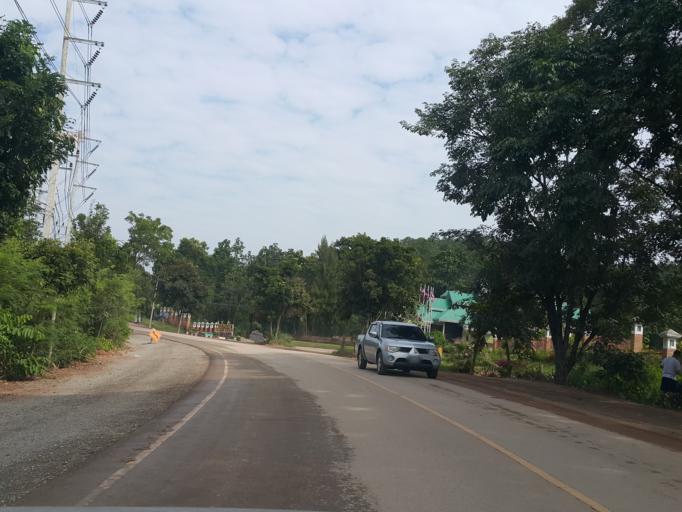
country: TH
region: Mae Hong Son
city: Mae Hong Son
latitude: 19.3343
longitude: 97.9660
